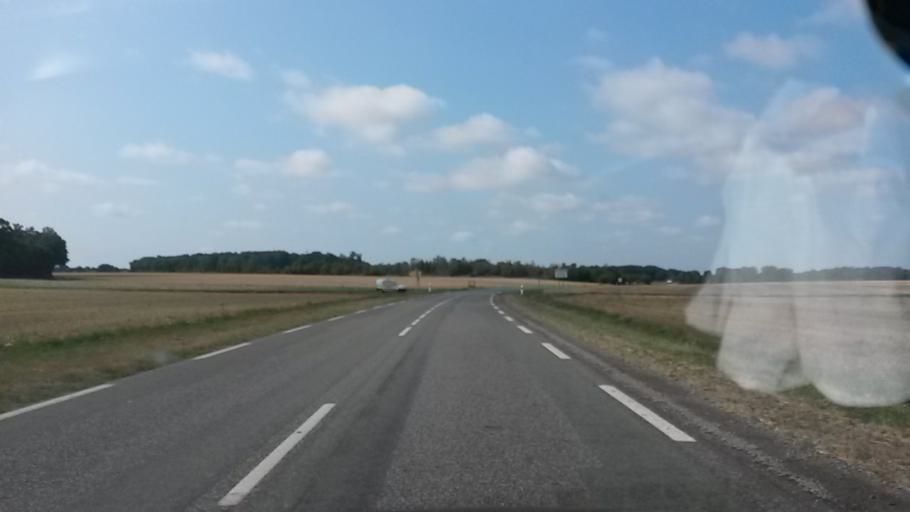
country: FR
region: Haute-Normandie
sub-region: Departement de l'Eure
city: Damville
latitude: 48.8301
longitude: 1.0187
